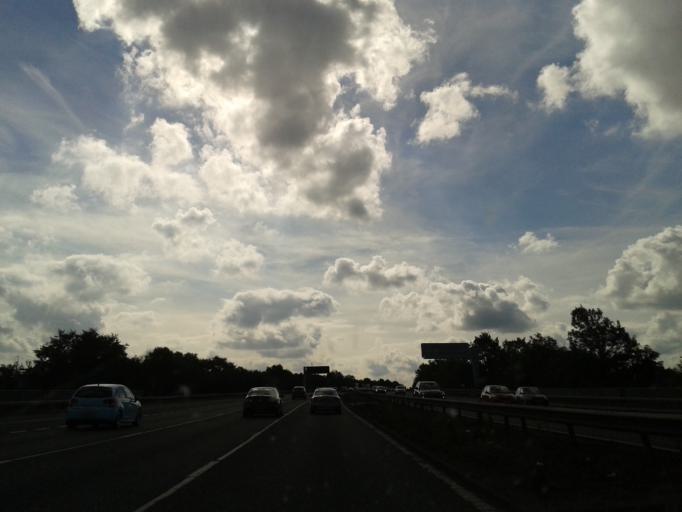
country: GB
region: England
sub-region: Staffordshire
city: Stafford
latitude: 52.8094
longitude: -2.1544
